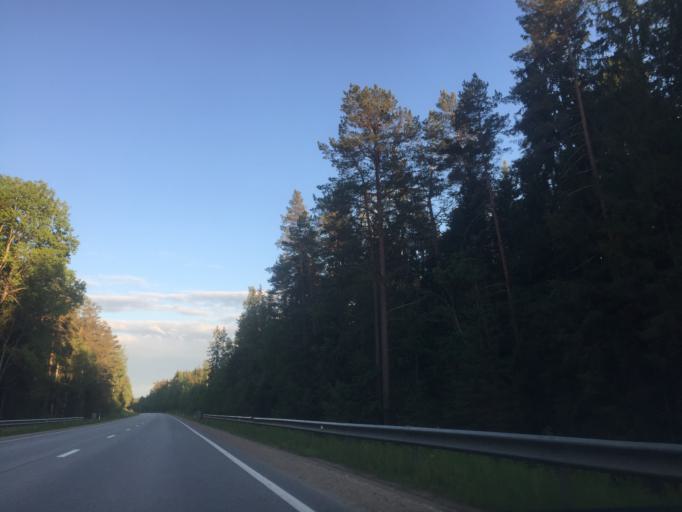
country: LV
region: Tukuma Rajons
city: Tukums
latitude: 57.0042
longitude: 23.0000
